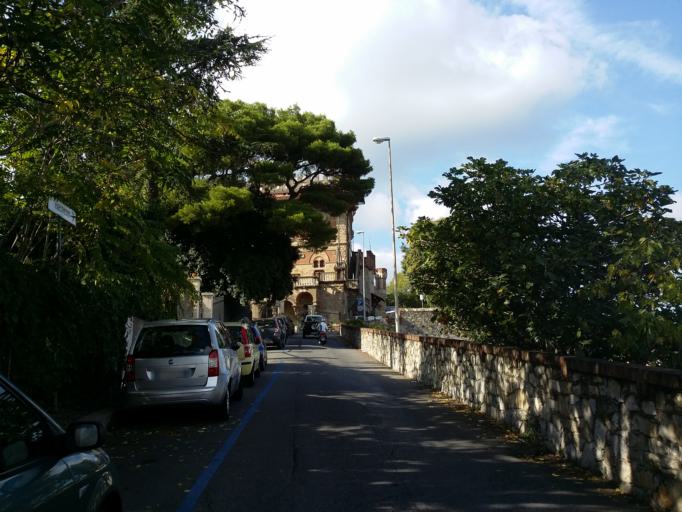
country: IT
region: Liguria
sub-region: Provincia di Genova
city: Genoa
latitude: 44.4149
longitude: 8.9476
